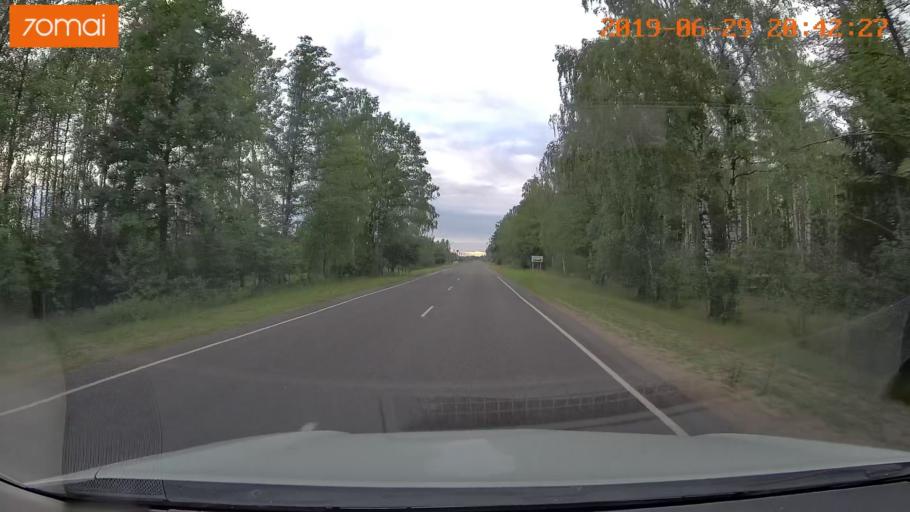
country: BY
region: Brest
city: Hantsavichy
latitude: 52.5976
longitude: 26.3258
